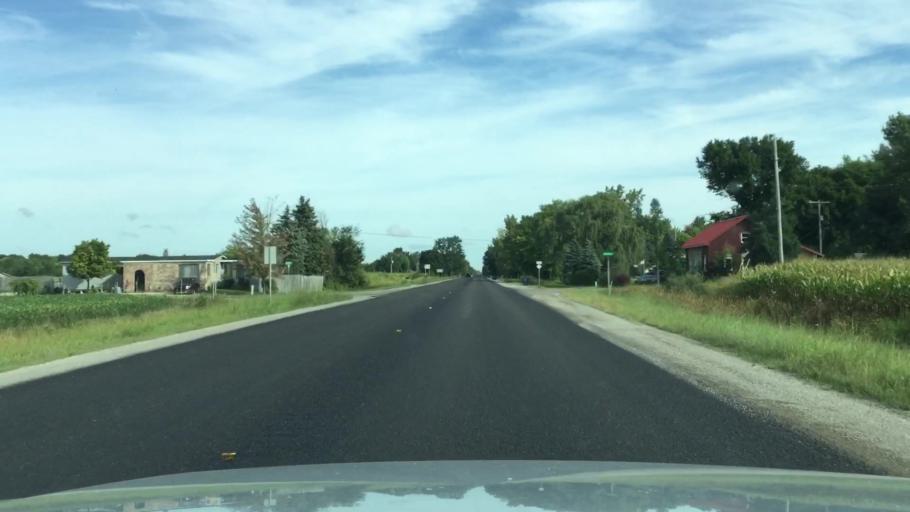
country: US
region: Michigan
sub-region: Genesee County
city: Montrose
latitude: 43.1466
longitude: -83.9295
